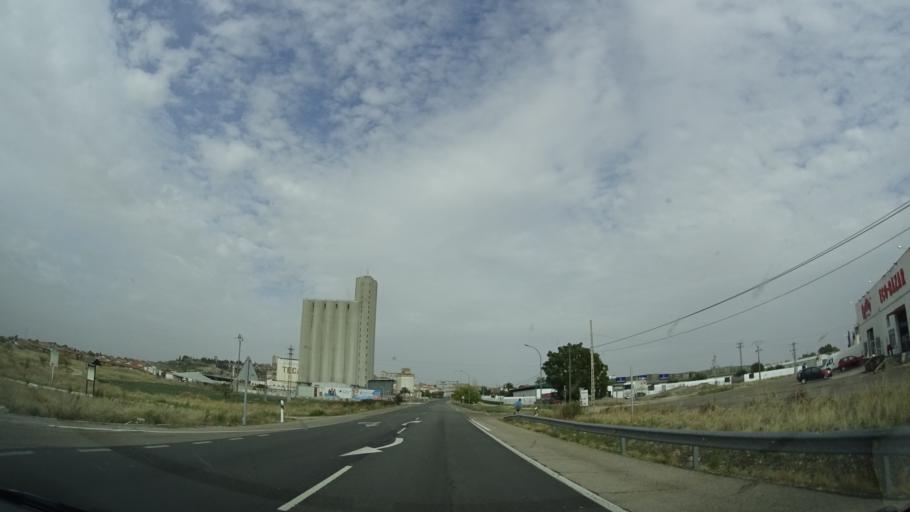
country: ES
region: Extremadura
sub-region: Provincia de Caceres
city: Trujillo
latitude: 39.4495
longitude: -5.8811
